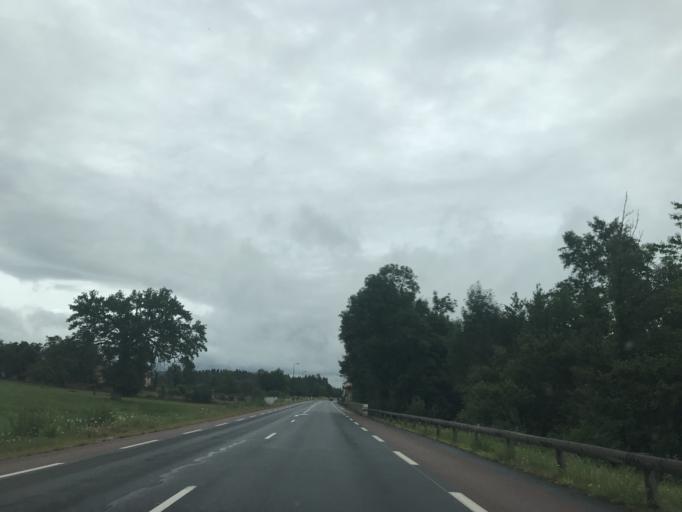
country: FR
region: Auvergne
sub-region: Departement du Puy-de-Dome
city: Arlanc
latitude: 45.4392
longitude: 3.7240
